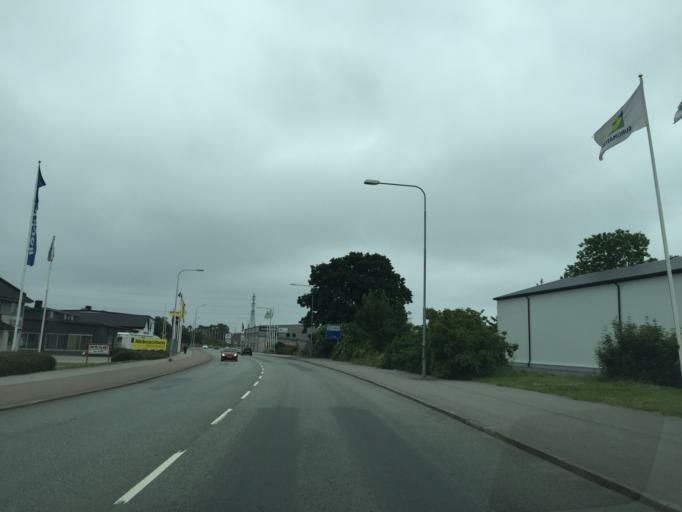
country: SE
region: Skane
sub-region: Ystads Kommun
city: Ystad
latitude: 55.4379
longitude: 13.8357
